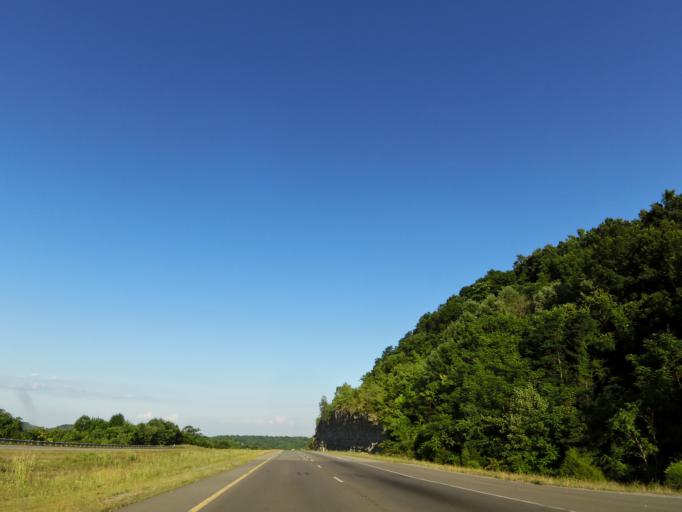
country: US
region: Tennessee
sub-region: Williamson County
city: Thompson's Station
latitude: 35.8136
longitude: -86.8003
